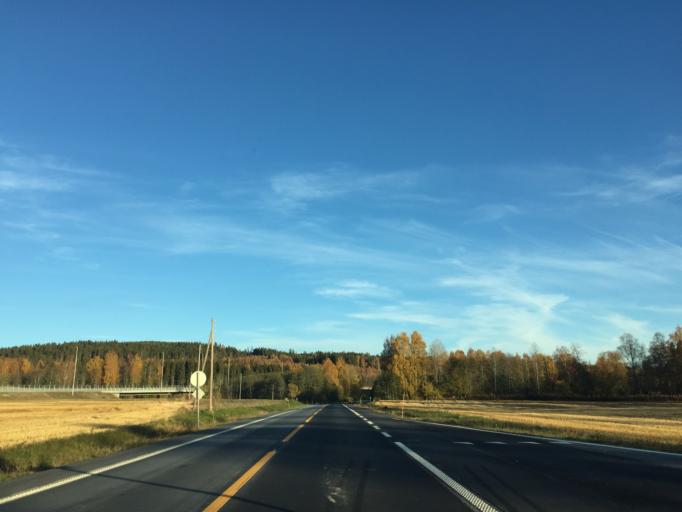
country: NO
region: Hedmark
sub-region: Kongsvinger
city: Spetalen
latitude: 60.2304
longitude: 11.8419
